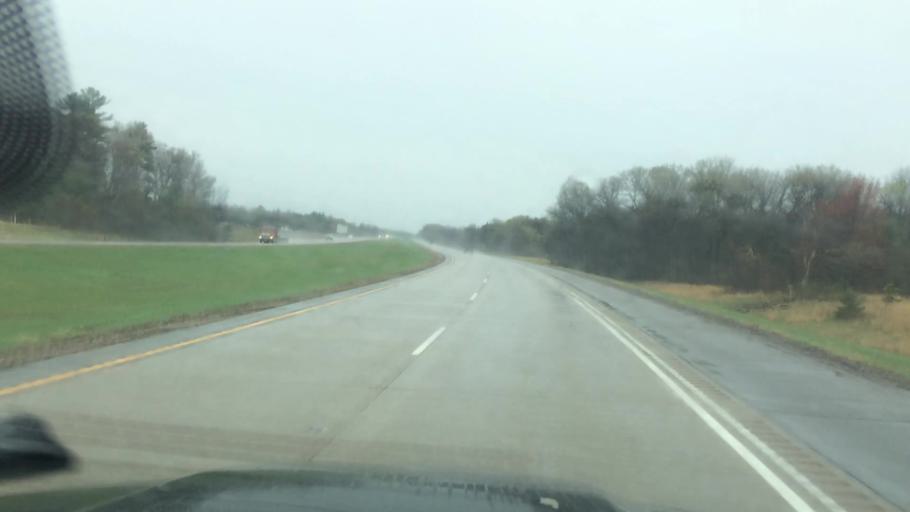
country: US
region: Wisconsin
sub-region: Marathon County
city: Mosinee
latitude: 44.6609
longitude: -89.6430
